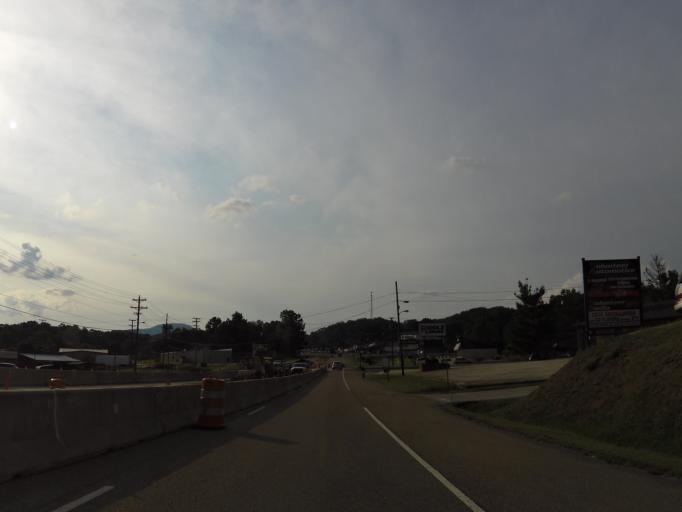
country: US
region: Tennessee
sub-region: Roane County
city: Oliver Springs
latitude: 36.0320
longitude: -84.3256
